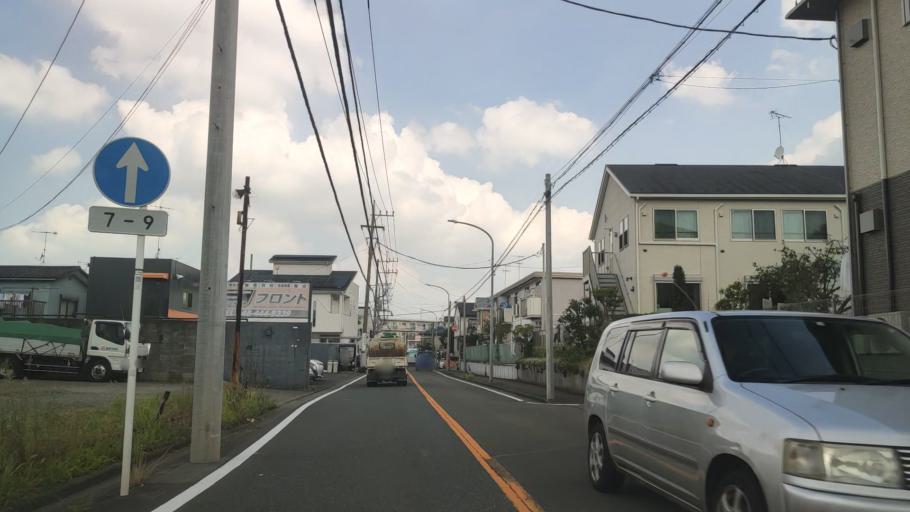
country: JP
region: Kanagawa
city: Minami-rinkan
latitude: 35.4556
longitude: 139.5012
